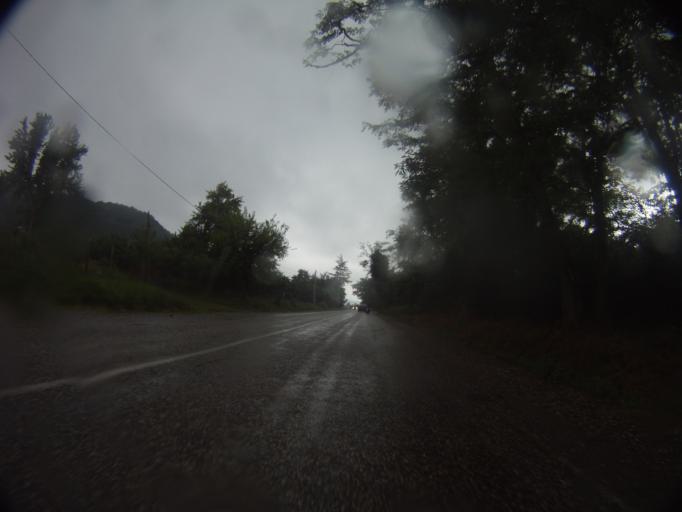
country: GE
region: Samegrelo and Zemo Svaneti
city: Jvari
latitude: 42.6873
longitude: 42.0356
